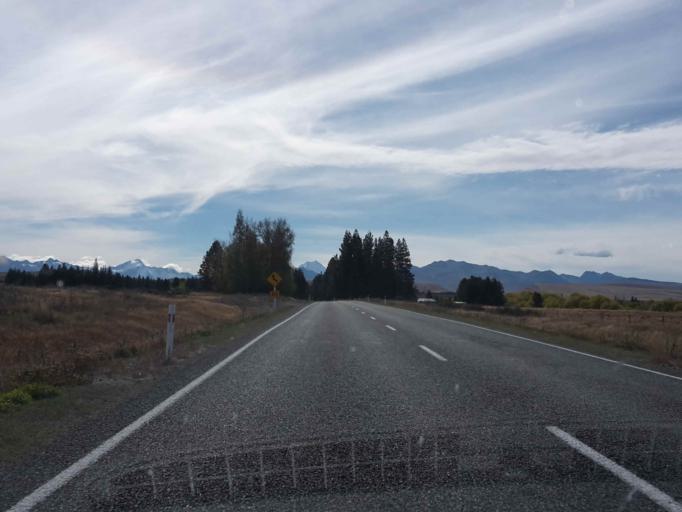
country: NZ
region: Canterbury
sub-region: Timaru District
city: Pleasant Point
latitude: -44.0929
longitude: 170.3514
